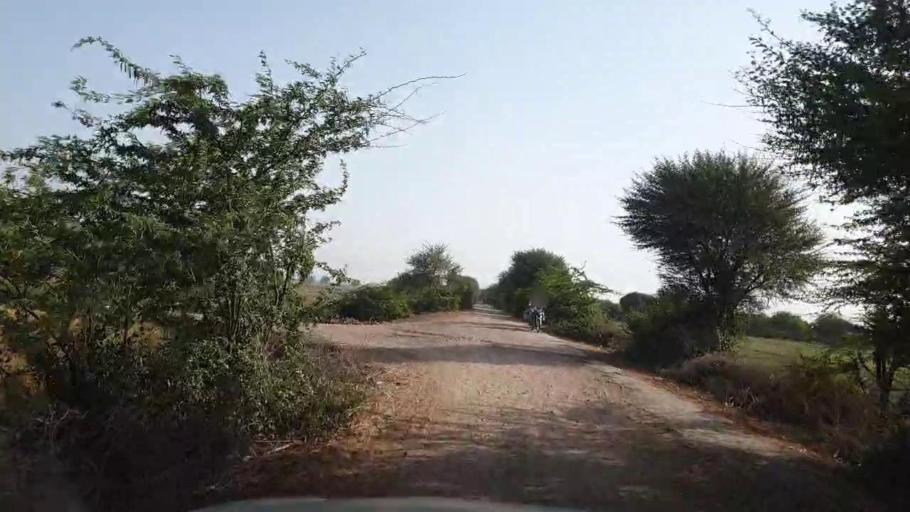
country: PK
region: Sindh
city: Tando Ghulam Ali
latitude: 25.0808
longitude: 68.8908
